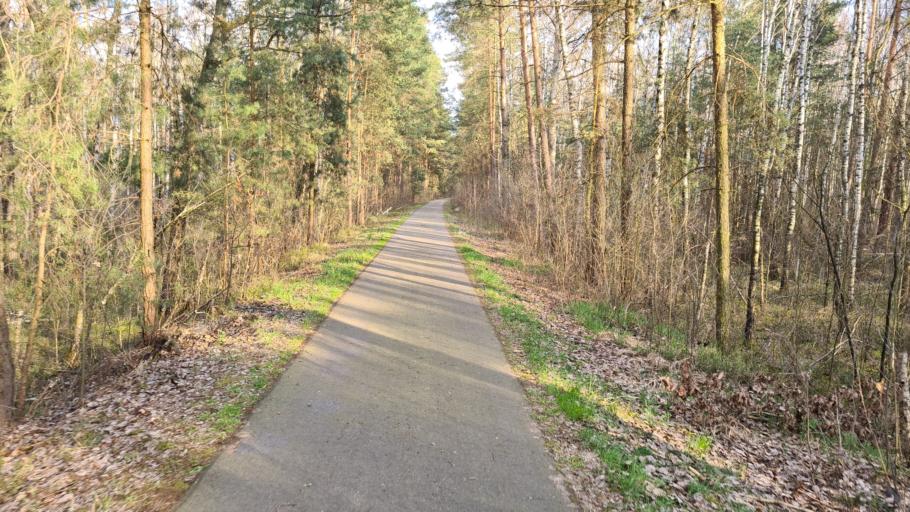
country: DE
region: Brandenburg
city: Schonborn
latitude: 51.5584
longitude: 13.5030
